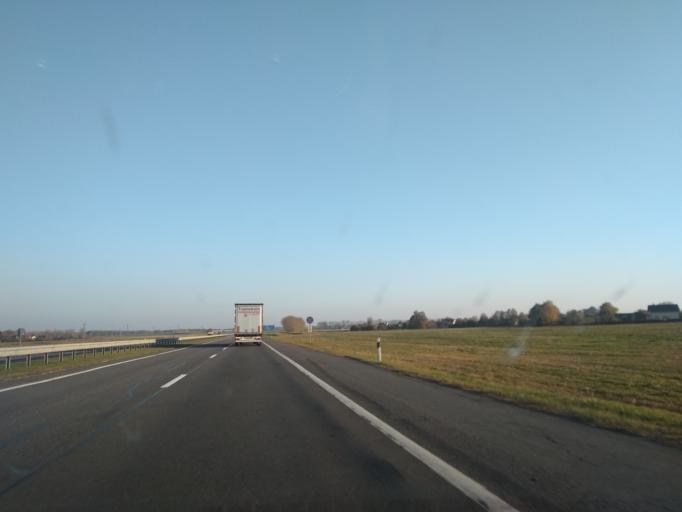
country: BY
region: Brest
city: Kobryn
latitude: 52.1919
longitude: 24.3087
